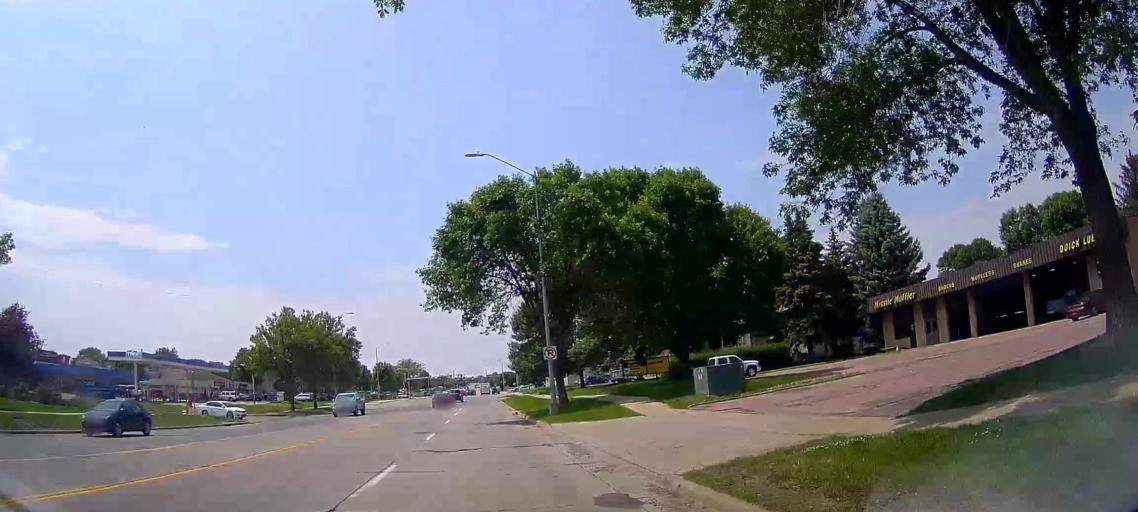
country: US
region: South Dakota
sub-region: Minnehaha County
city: Sioux Falls
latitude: 43.5077
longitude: -96.7682
